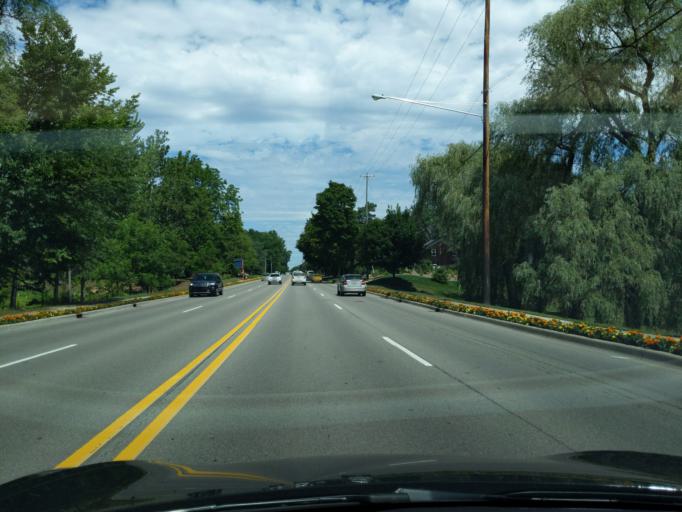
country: US
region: Michigan
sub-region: Midland County
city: Midland
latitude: 43.6268
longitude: -84.2470
